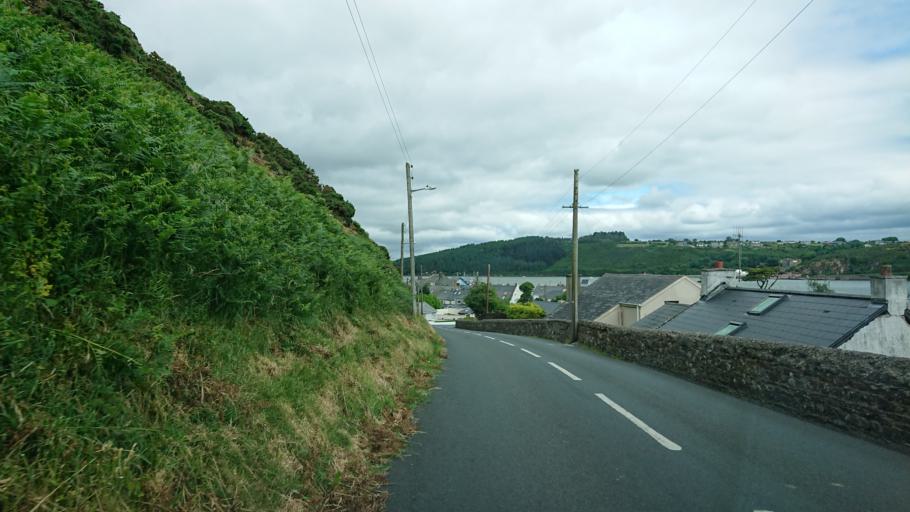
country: IE
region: Munster
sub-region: Waterford
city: Dunmore East
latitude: 52.2370
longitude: -6.9719
